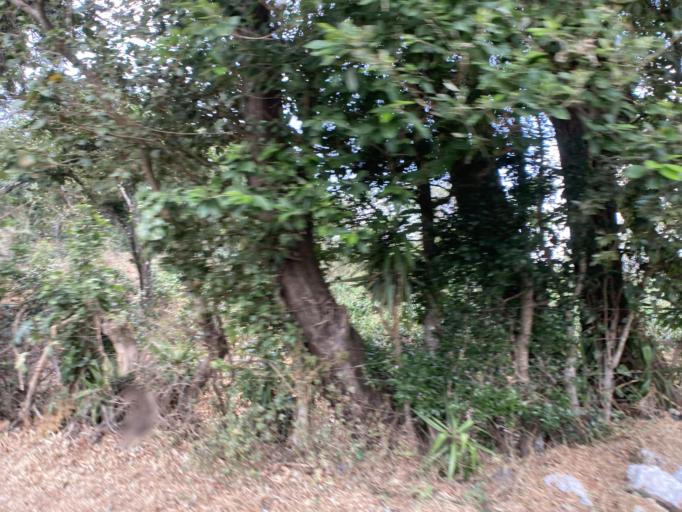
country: GT
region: Escuintla
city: San Vicente Pacaya
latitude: 14.3506
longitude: -90.5724
